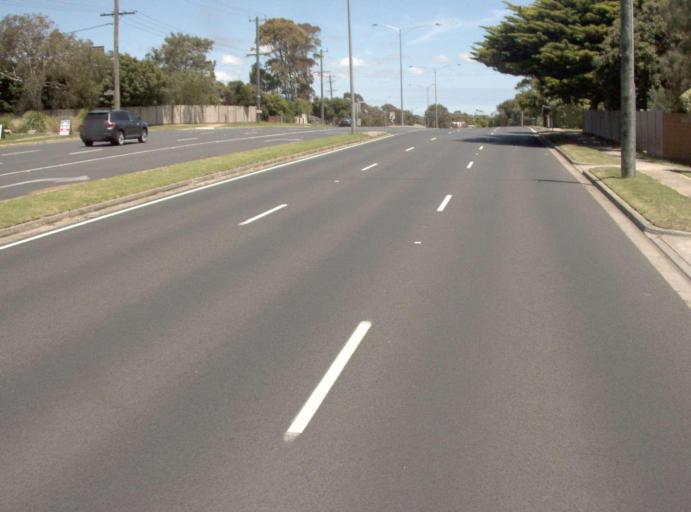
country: AU
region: Victoria
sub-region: Mornington Peninsula
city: Mornington
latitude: -38.2347
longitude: 145.0379
